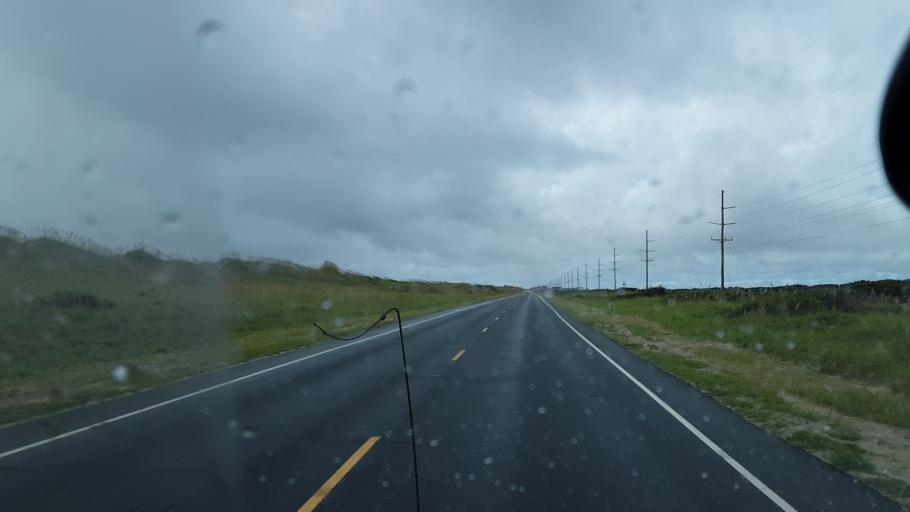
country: US
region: North Carolina
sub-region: Dare County
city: Buxton
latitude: 35.2231
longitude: -75.6473
